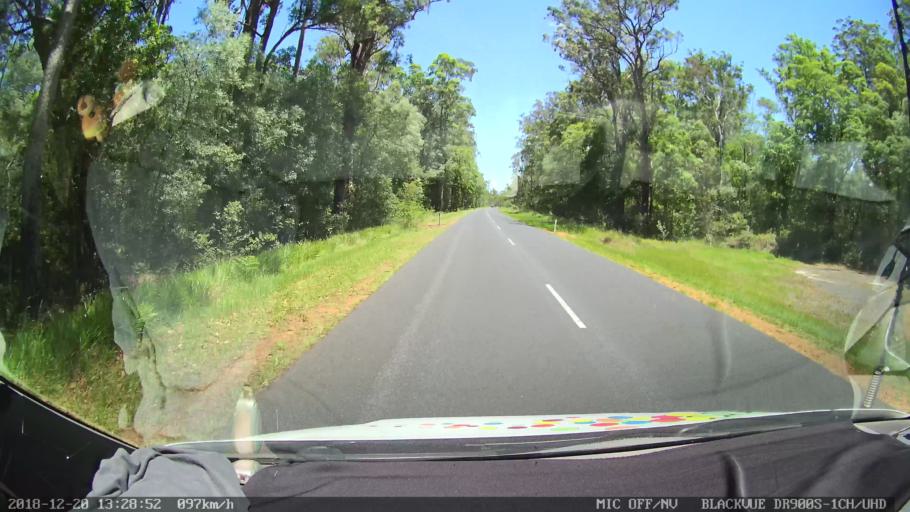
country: AU
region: New South Wales
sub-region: Clarence Valley
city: Gordon
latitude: -29.1808
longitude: 152.9893
